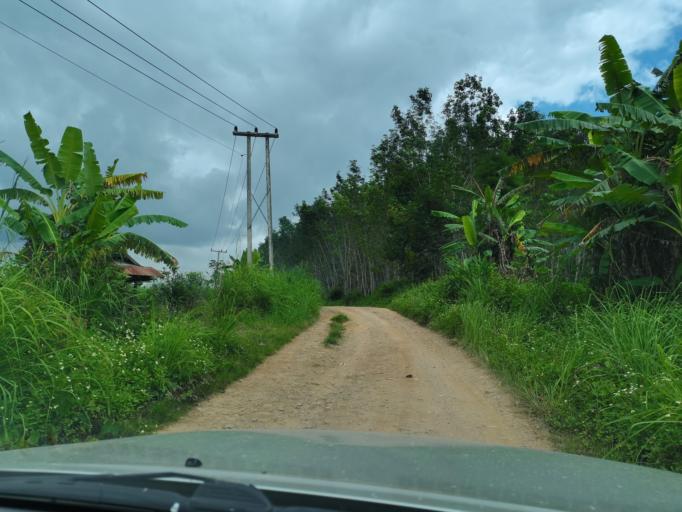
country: LA
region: Loungnamtha
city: Muang Long
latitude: 20.6987
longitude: 101.0365
